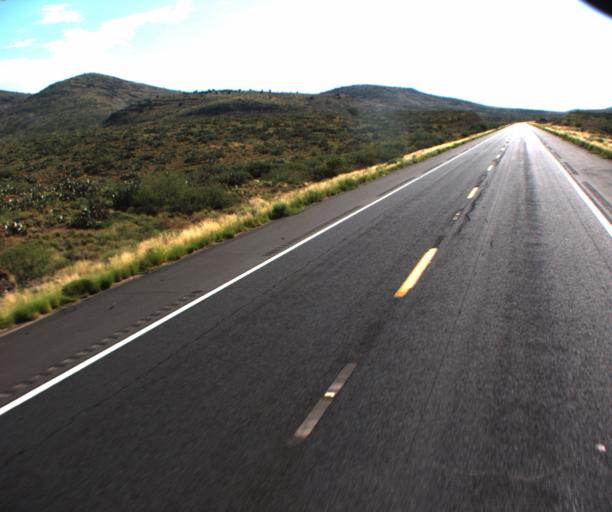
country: US
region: Arizona
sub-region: Greenlee County
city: Clifton
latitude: 32.8514
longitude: -109.3320
